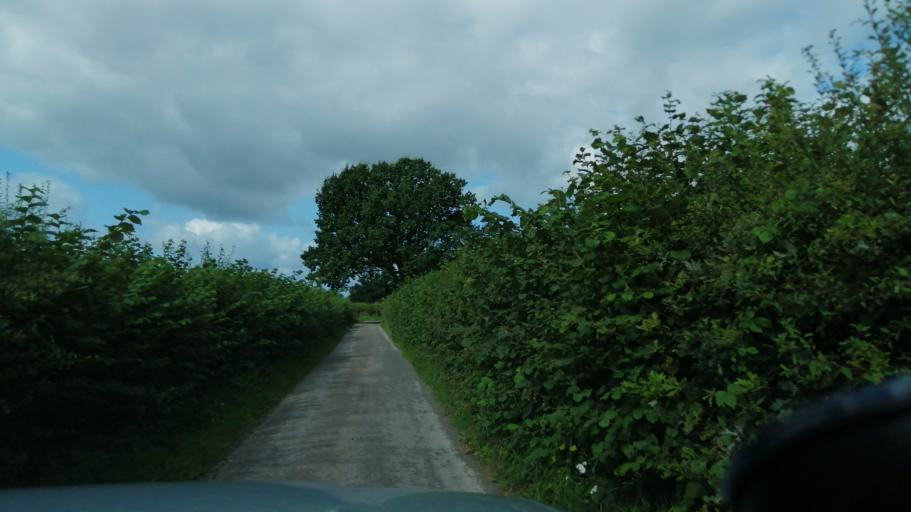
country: GB
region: England
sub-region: Herefordshire
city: Kinnersley
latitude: 52.1331
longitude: -2.9419
